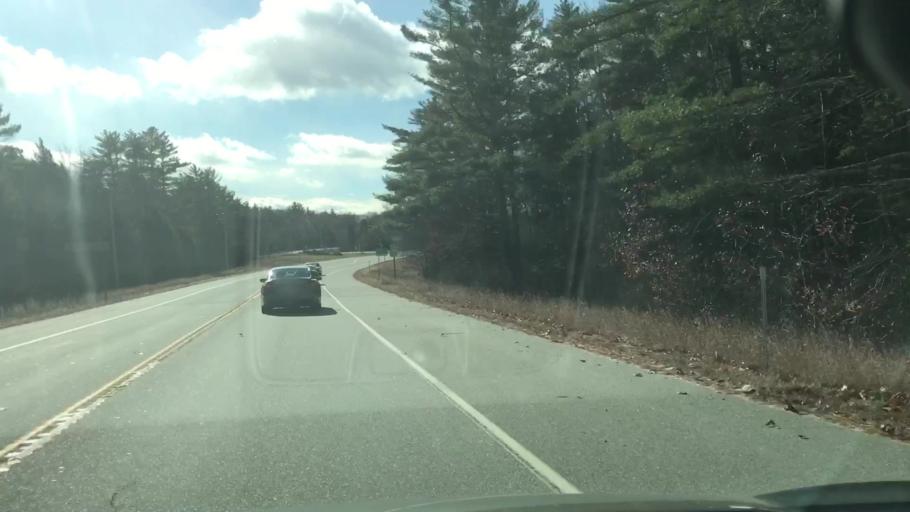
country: US
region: New Hampshire
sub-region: Belknap County
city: Barnstead
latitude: 43.3468
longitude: -71.2654
